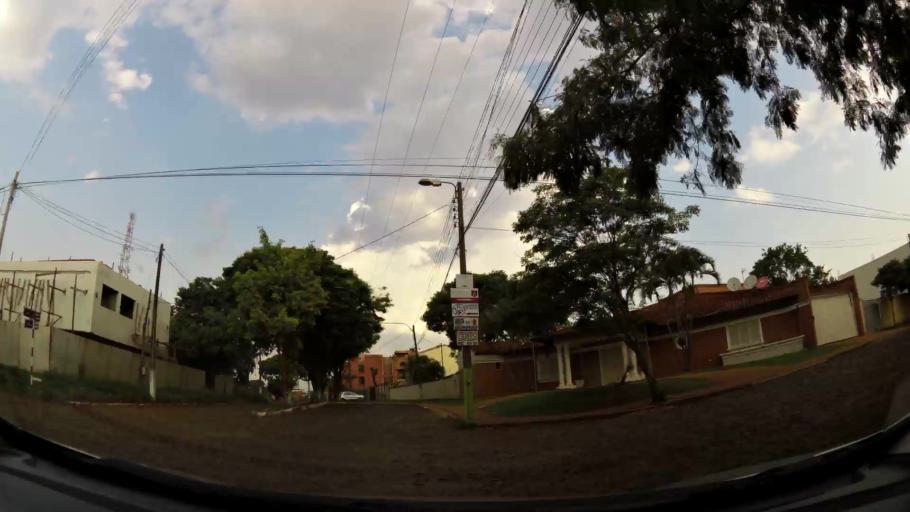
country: PY
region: Alto Parana
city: Presidente Franco
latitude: -25.5203
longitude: -54.6305
